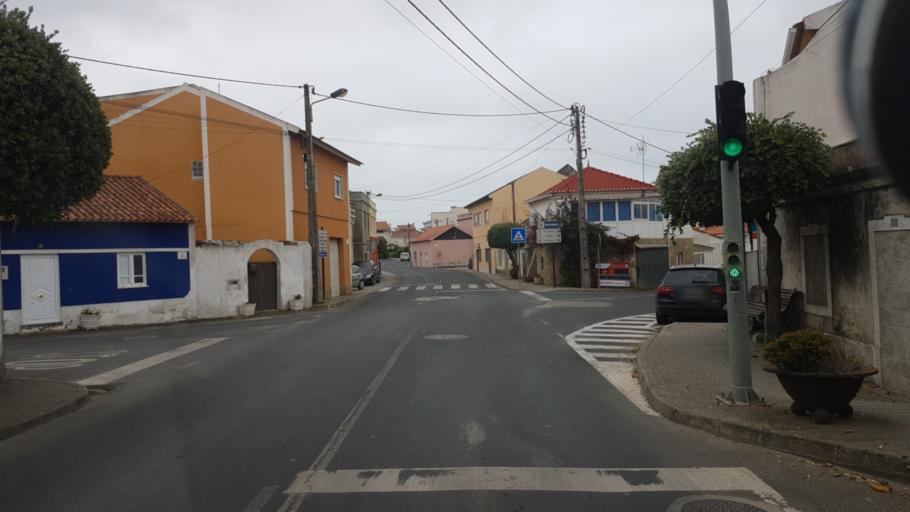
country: PT
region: Lisbon
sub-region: Lourinha
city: Lourinha
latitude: 39.2028
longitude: -9.3284
